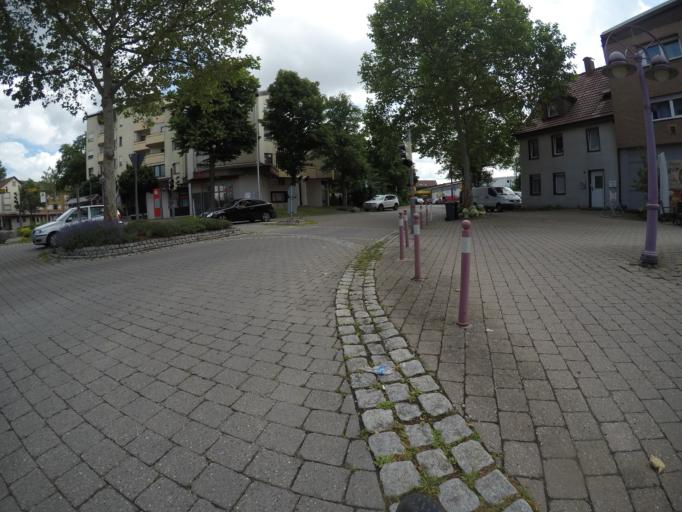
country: DE
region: Baden-Wuerttemberg
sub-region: Regierungsbezirk Stuttgart
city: Salach
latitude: 48.6901
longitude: 9.7370
